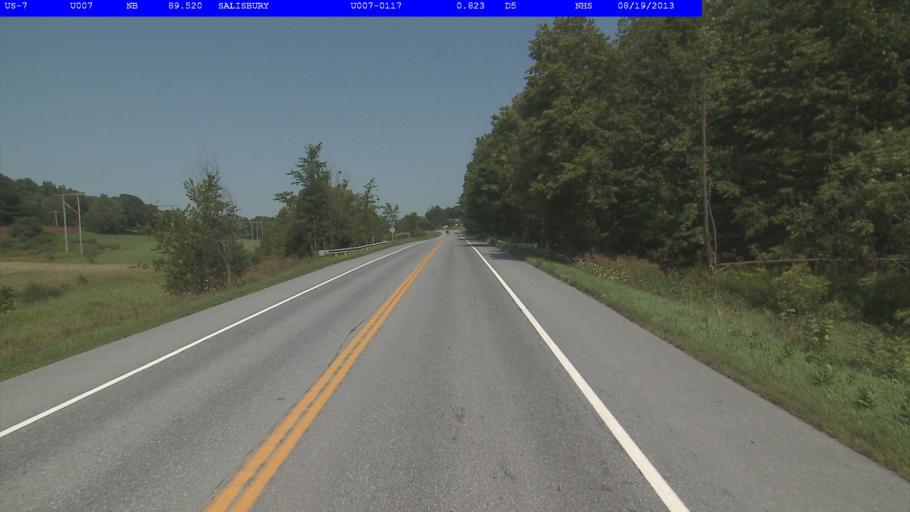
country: US
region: Vermont
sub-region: Rutland County
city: Brandon
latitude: 43.9037
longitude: -73.1102
